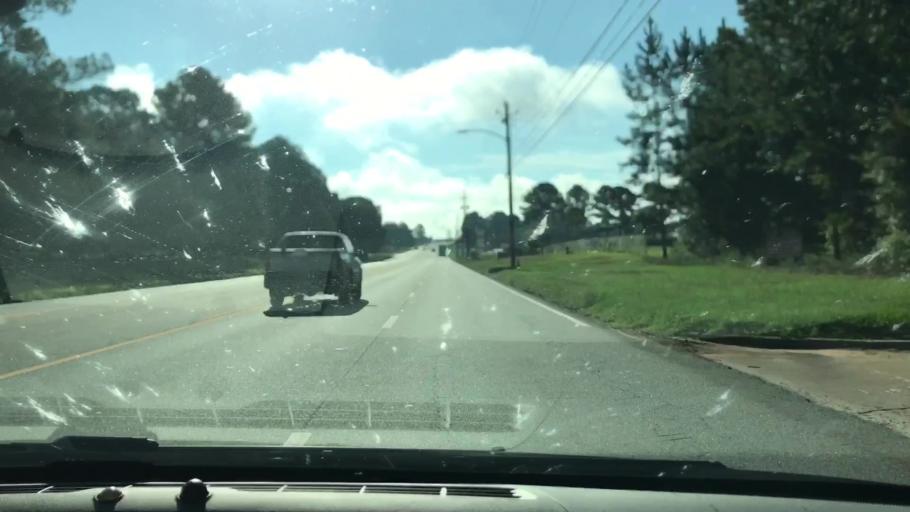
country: US
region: Georgia
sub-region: Terrell County
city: Dawson
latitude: 31.7630
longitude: -84.4428
